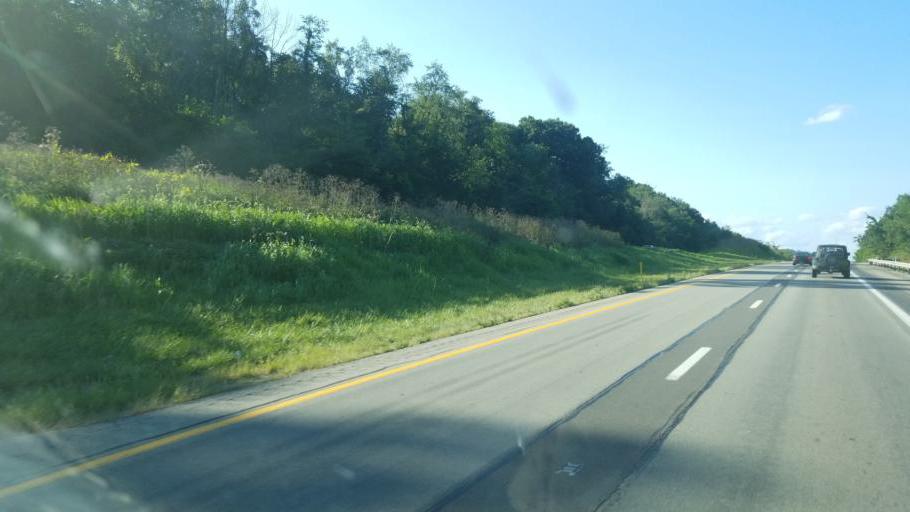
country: US
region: Pennsylvania
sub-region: Washington County
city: East Washington
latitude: 40.0869
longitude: -80.1928
